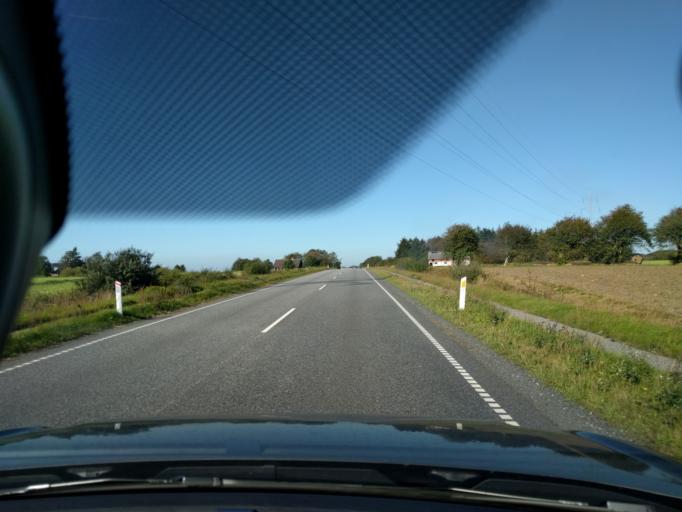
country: DK
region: North Denmark
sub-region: Vesthimmerland Kommune
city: Alestrup
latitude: 56.7276
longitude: 9.6062
